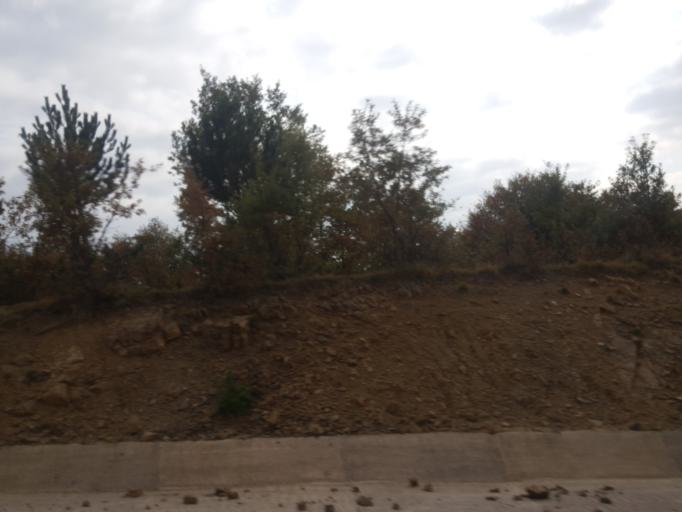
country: TR
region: Sinop
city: Duragan
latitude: 41.4917
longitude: 35.0318
